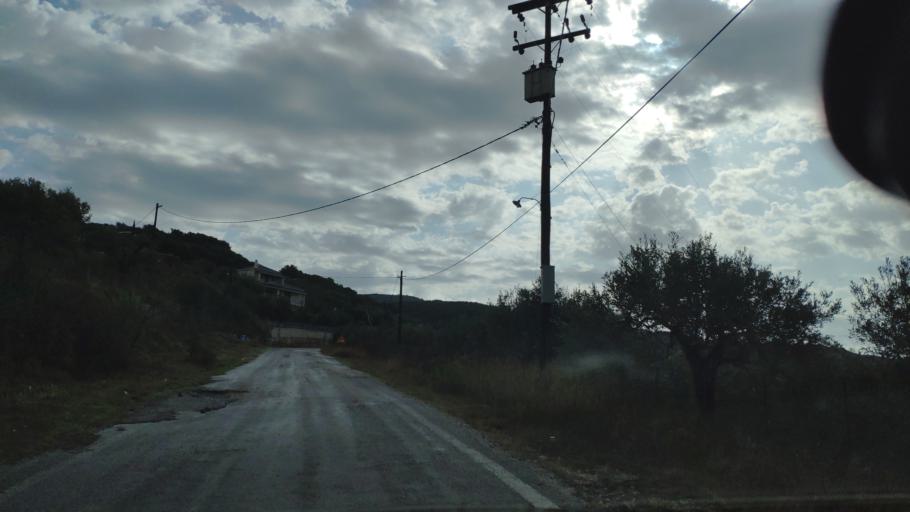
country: GR
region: West Greece
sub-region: Nomos Aitolias kai Akarnanias
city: Sardinia
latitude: 38.8902
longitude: 21.2262
